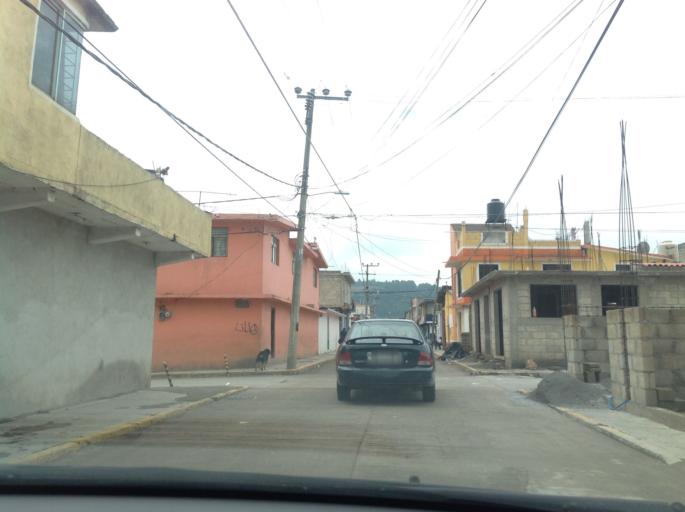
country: MX
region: Morelos
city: Joquicingo de Leon Guzman
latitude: 19.0512
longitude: -99.5334
